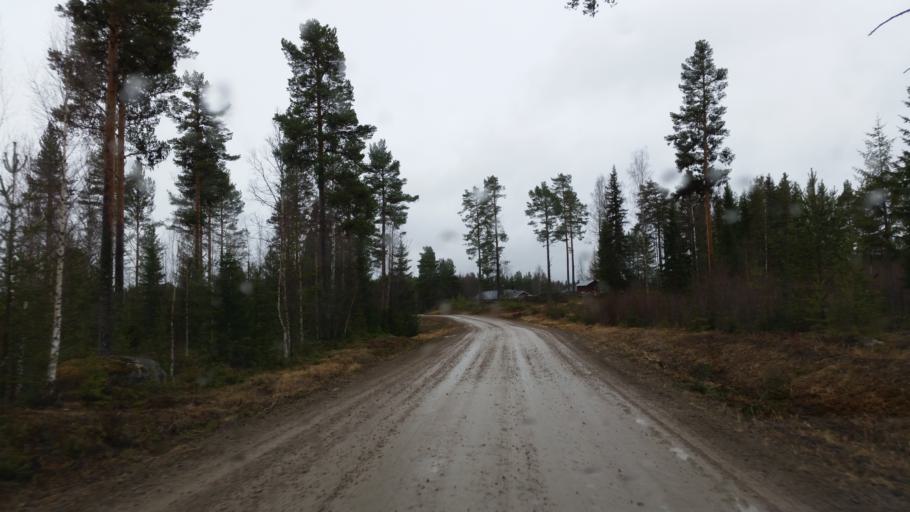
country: SE
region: Vaesternorrland
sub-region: Ange Kommun
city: Ange
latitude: 62.1492
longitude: 15.6604
